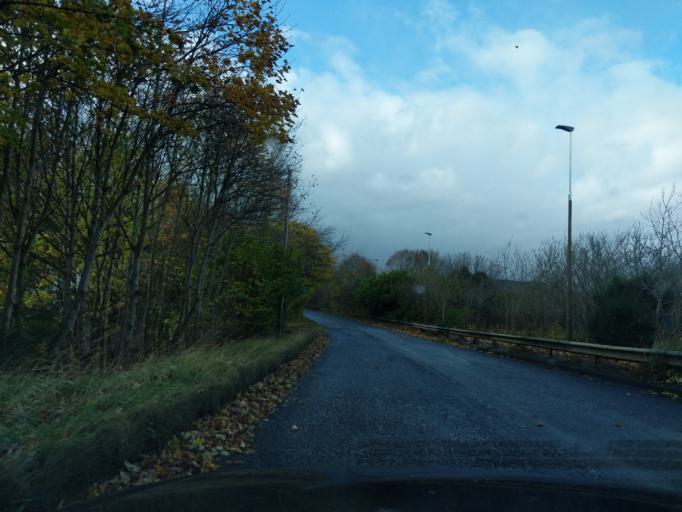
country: GB
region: Scotland
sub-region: Edinburgh
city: Newbridge
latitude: 55.9352
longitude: -3.3936
